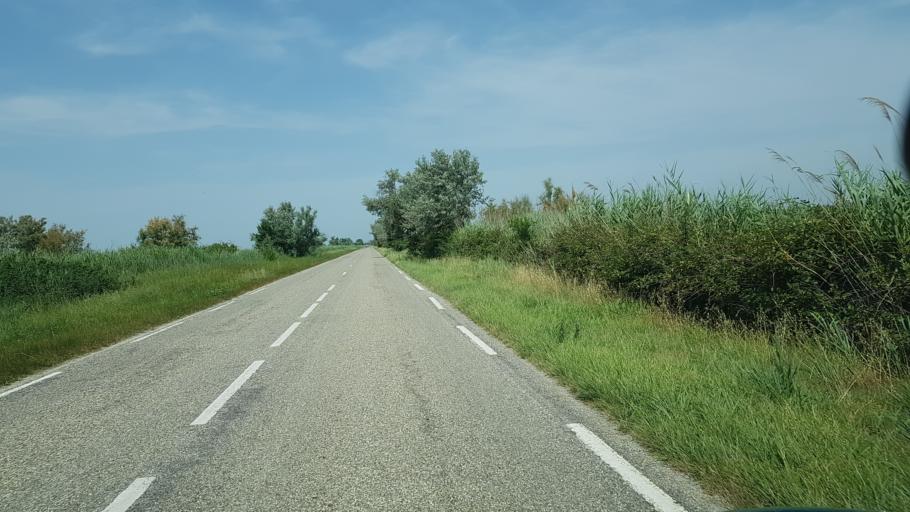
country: FR
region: Languedoc-Roussillon
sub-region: Departement du Gard
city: Saint-Gilles
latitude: 43.5741
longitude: 4.5255
